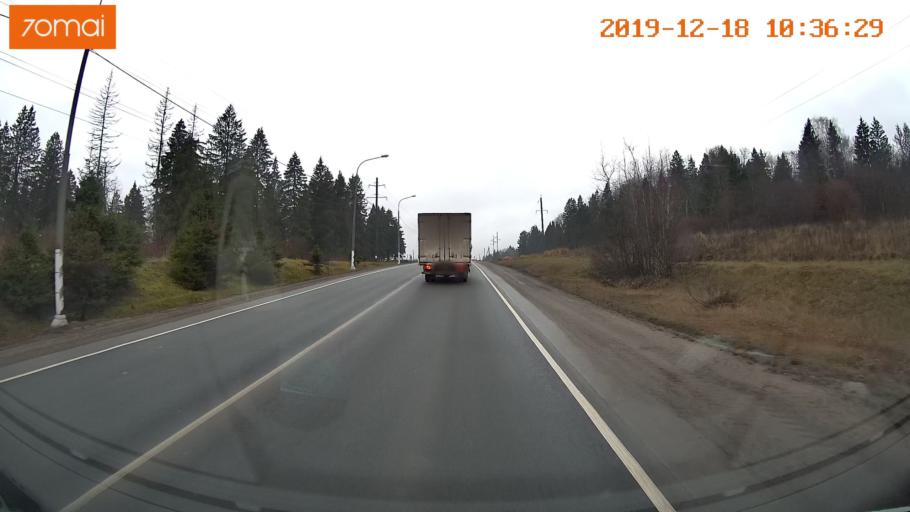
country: RU
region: Moskovskaya
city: Troitsk
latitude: 55.4210
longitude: 37.1844
